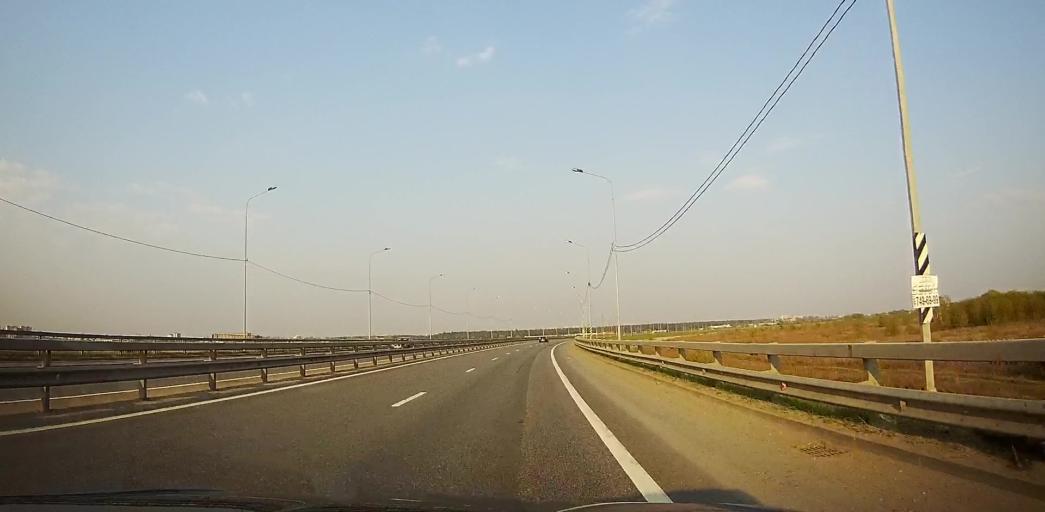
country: RU
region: Moskovskaya
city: Zhukovskiy
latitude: 55.5786
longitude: 38.0823
